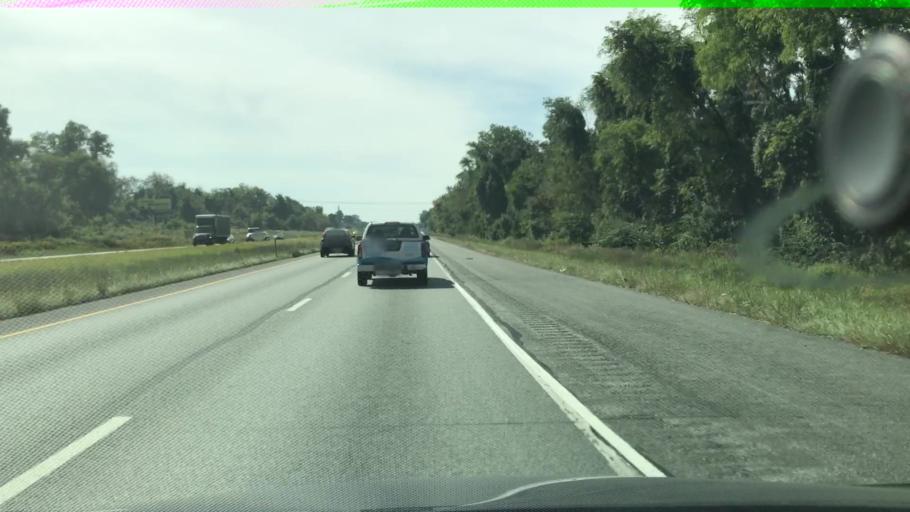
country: US
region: Pennsylvania
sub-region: York County
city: Hallam
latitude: 40.0043
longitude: -76.6229
